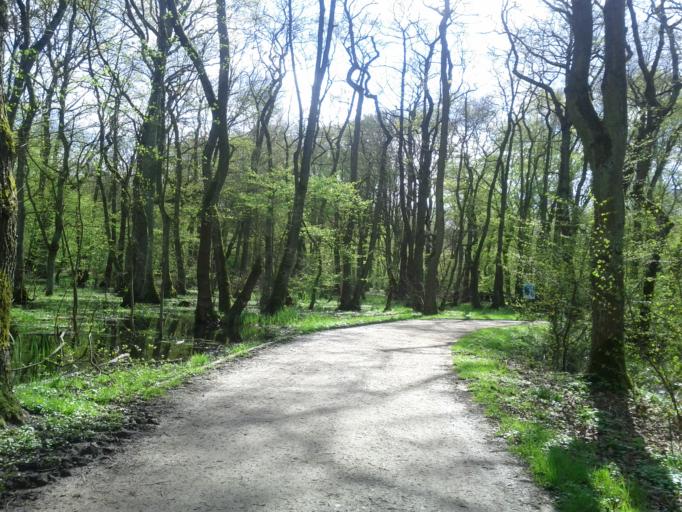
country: DE
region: North Rhine-Westphalia
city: Lanstrop
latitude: 51.5512
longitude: 7.5621
